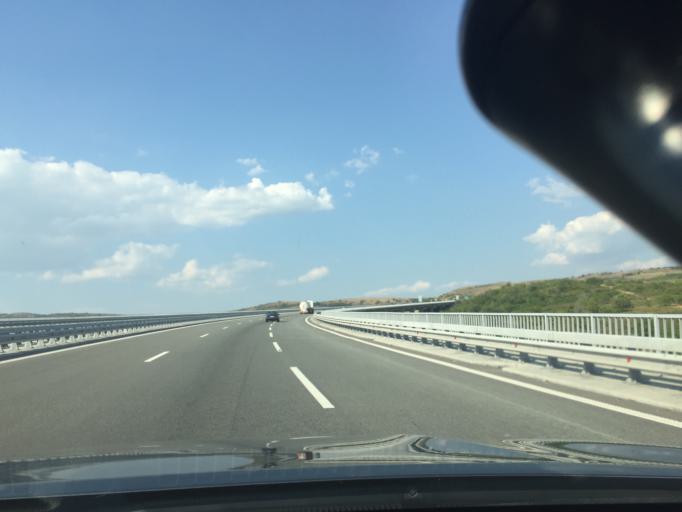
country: BG
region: Kyustendil
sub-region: Obshtina Dupnitsa
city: Dupnitsa
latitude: 42.2671
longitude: 23.0692
